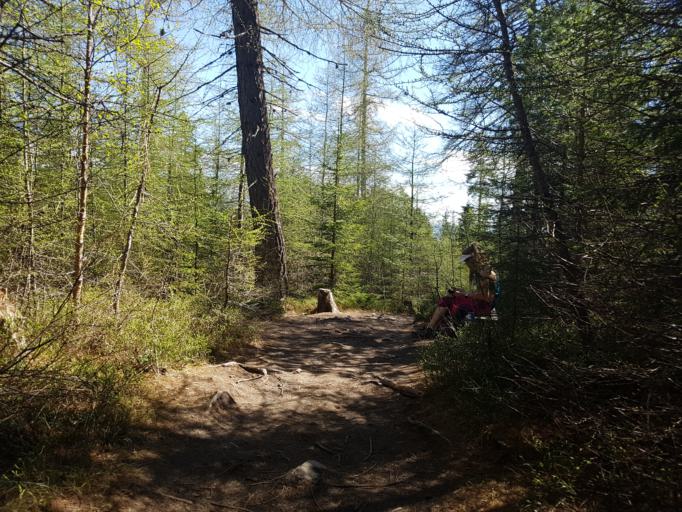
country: NO
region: Sor-Trondelag
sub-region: Trondheim
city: Trondheim
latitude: 63.4276
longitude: 10.3142
